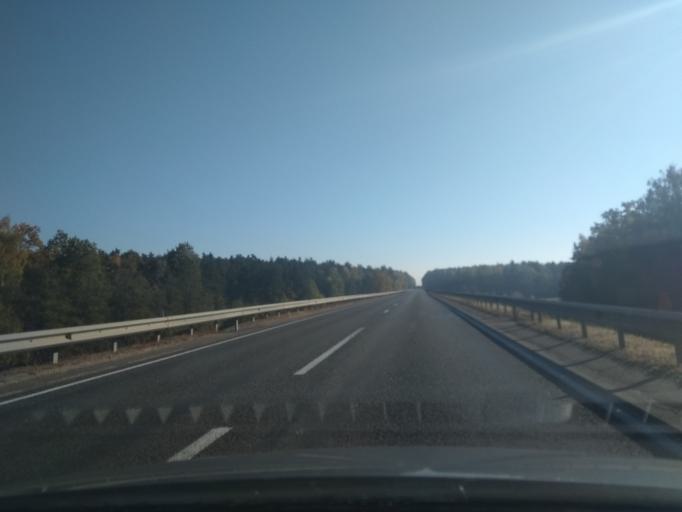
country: BY
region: Grodnenskaya
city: Zel'va
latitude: 53.1393
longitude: 24.9203
